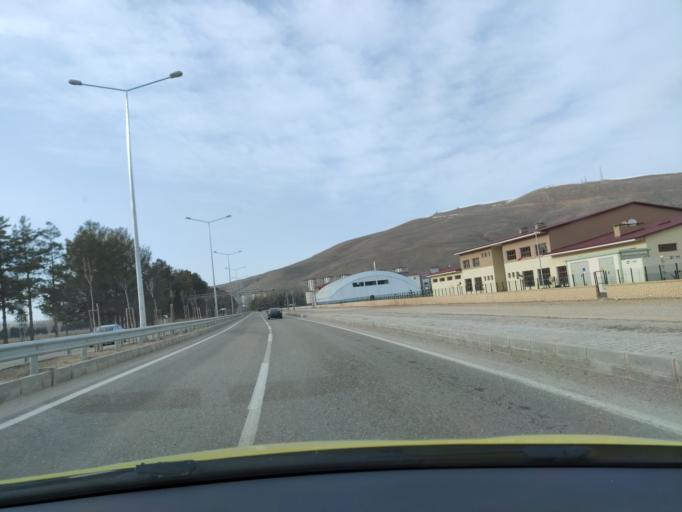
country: TR
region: Bayburt
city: Bayburt
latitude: 40.2336
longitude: 40.2556
